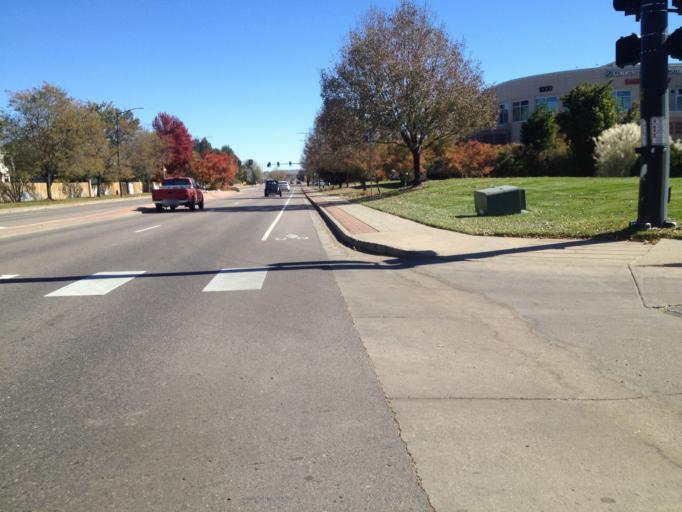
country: US
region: Colorado
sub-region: Boulder County
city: Lafayette
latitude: 39.9868
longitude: -105.1035
